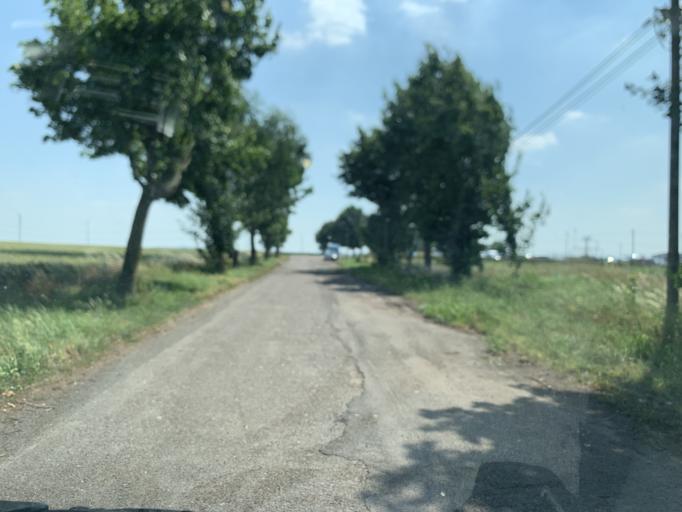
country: DE
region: Saxony-Anhalt
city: Erxleben
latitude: 52.1751
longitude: 11.2599
